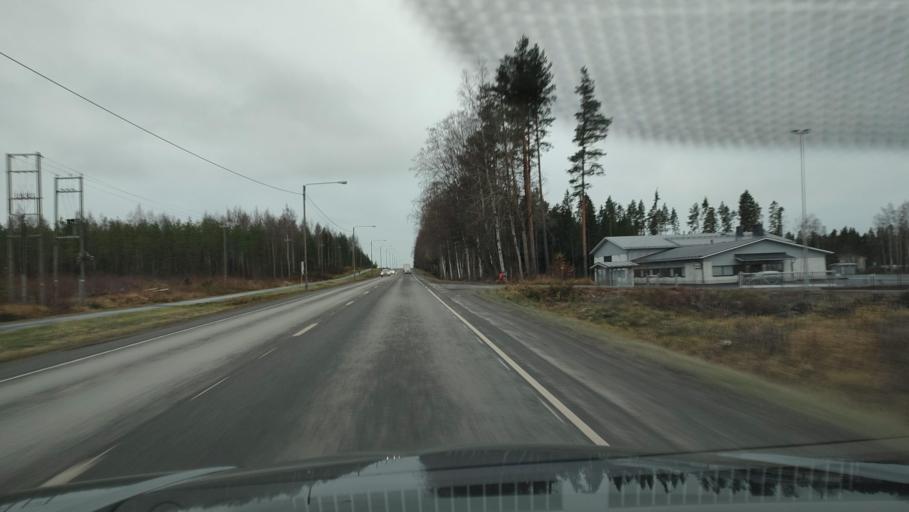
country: FI
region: Southern Ostrobothnia
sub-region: Seinaejoki
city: Seinaejoki
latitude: 62.7837
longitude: 22.7110
